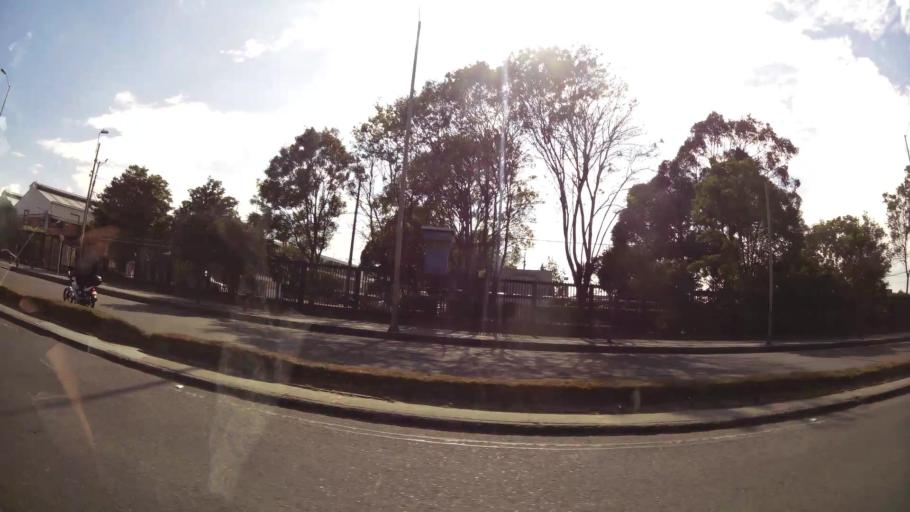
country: CO
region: Bogota D.C.
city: Bogota
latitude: 4.5825
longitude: -74.1432
